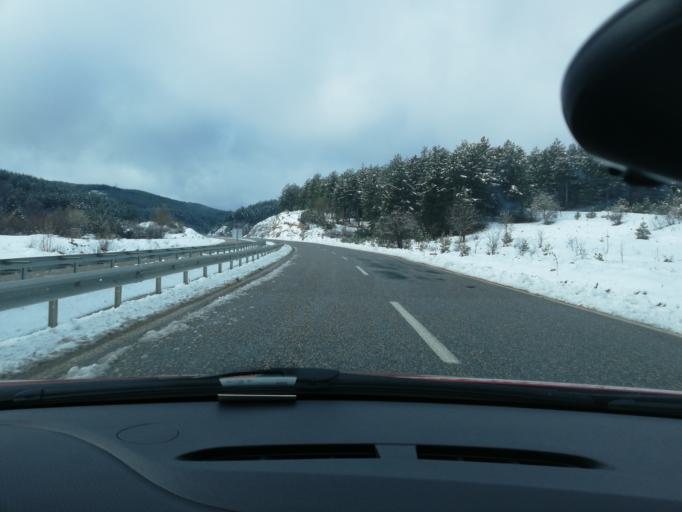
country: TR
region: Kastamonu
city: Akkaya
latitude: 41.2849
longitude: 33.4345
